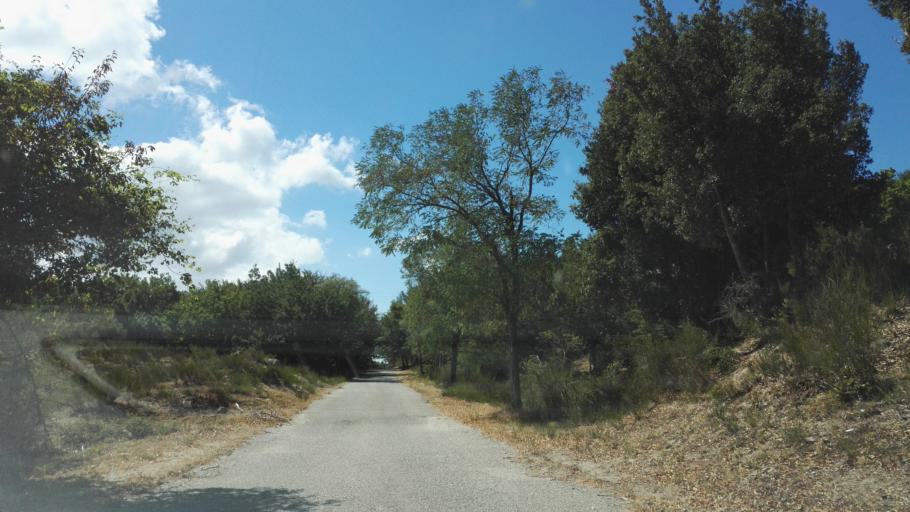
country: IT
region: Calabria
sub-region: Provincia di Vibo-Valentia
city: Nardodipace
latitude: 38.4871
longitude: 16.3702
